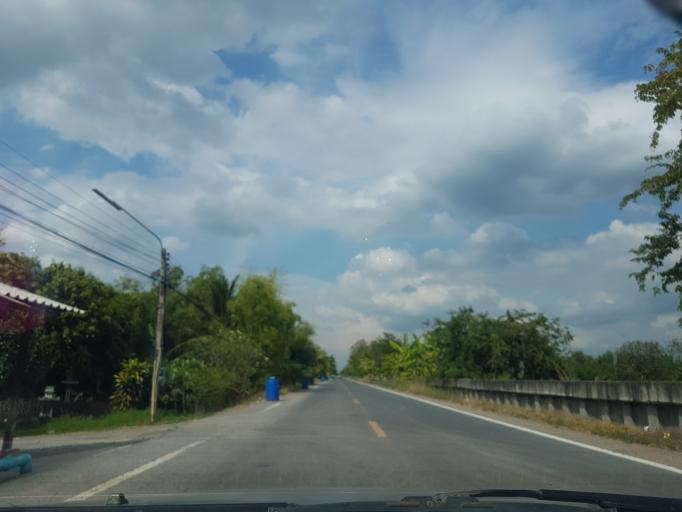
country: TH
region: Pathum Thani
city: Nong Suea
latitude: 14.1679
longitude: 100.8915
